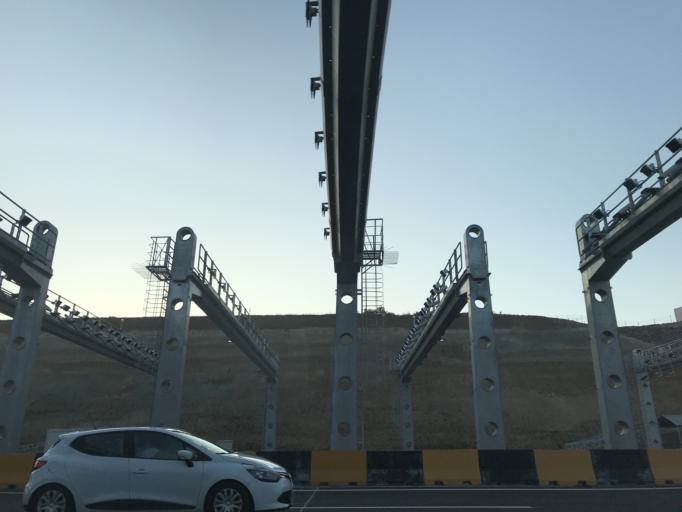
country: TR
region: Kocaeli
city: Tavsanli
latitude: 40.8047
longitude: 29.5199
